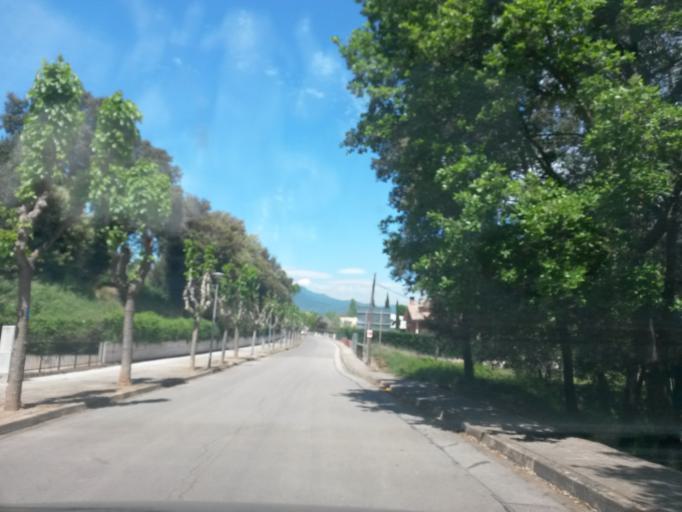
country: ES
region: Catalonia
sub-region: Provincia de Girona
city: Vilablareix
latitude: 41.9641
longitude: 2.7634
